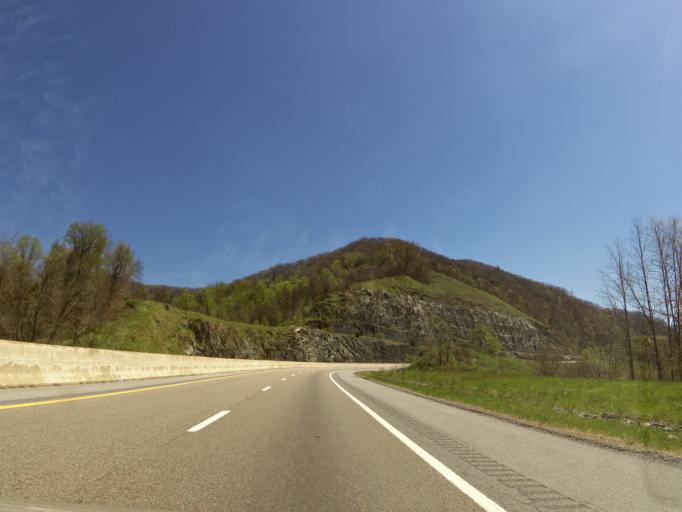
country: US
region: North Carolina
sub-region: Madison County
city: Mars Hill
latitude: 35.9879
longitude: -82.5432
